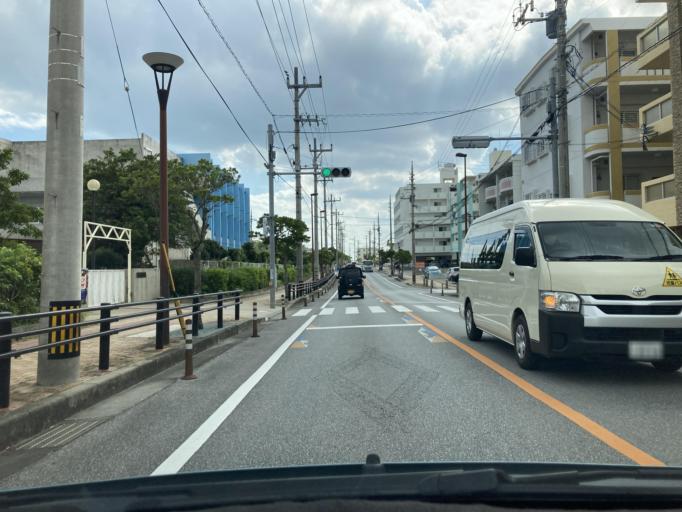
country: JP
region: Okinawa
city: Ginowan
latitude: 26.2485
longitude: 127.7733
